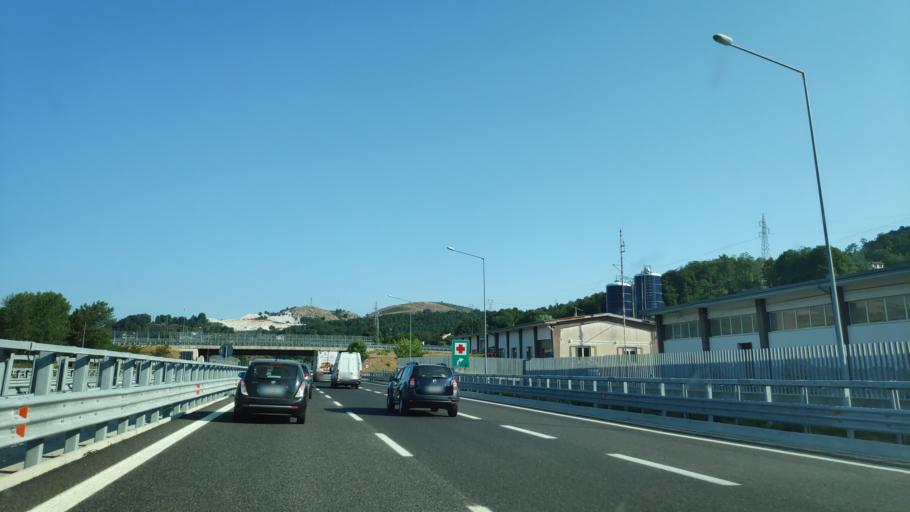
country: IT
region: Basilicate
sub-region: Provincia di Potenza
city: Lagonegro
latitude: 40.1332
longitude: 15.7614
